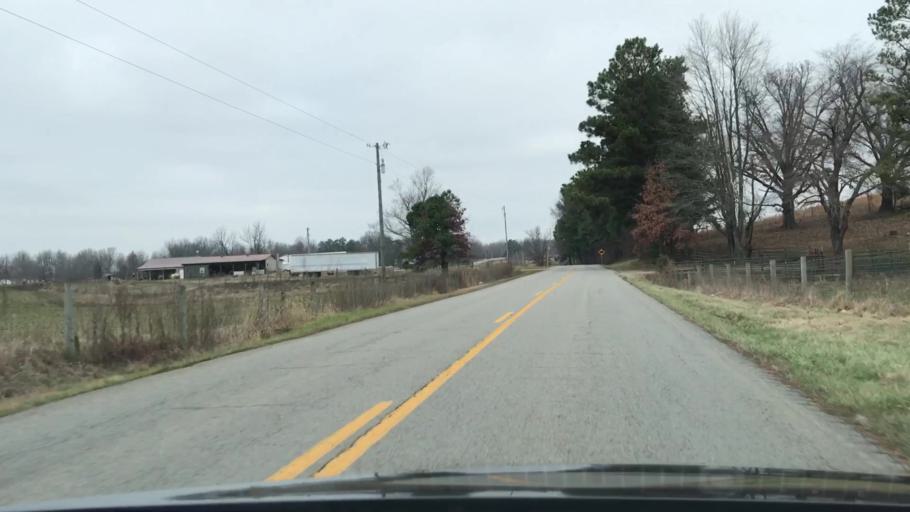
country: US
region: Kentucky
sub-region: McLean County
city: Calhoun
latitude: 37.4790
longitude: -87.2457
